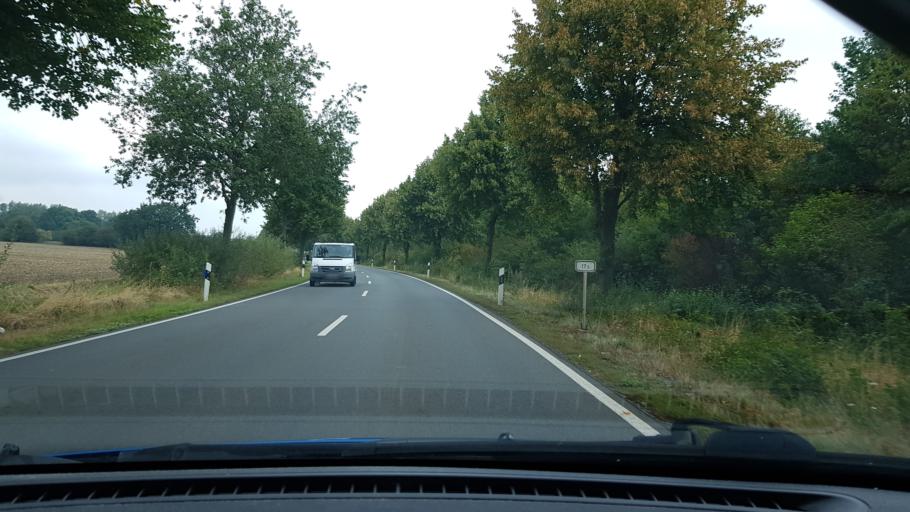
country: DE
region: Lower Saxony
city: Grossgoltern
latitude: 52.3278
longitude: 9.4696
